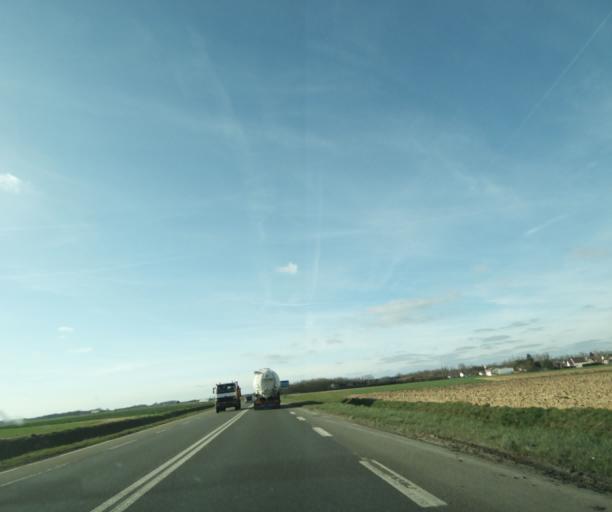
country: FR
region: Ile-de-France
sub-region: Departement des Yvelines
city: Ablis
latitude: 48.5121
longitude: 1.8293
